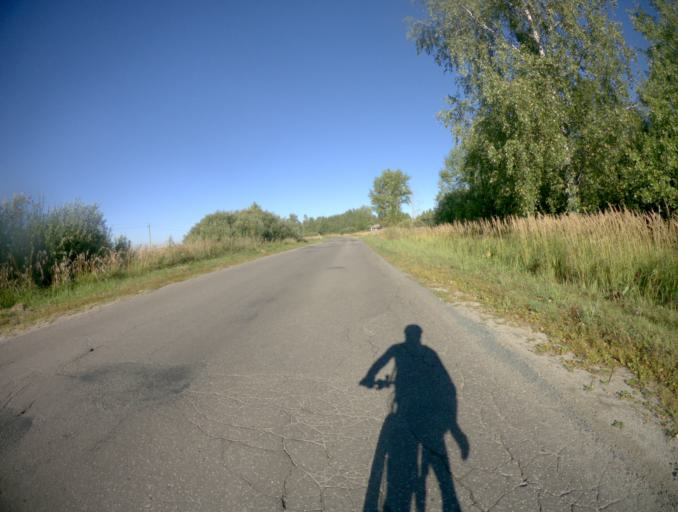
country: RU
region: Vladimir
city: Luknovo
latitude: 56.2218
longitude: 42.0244
